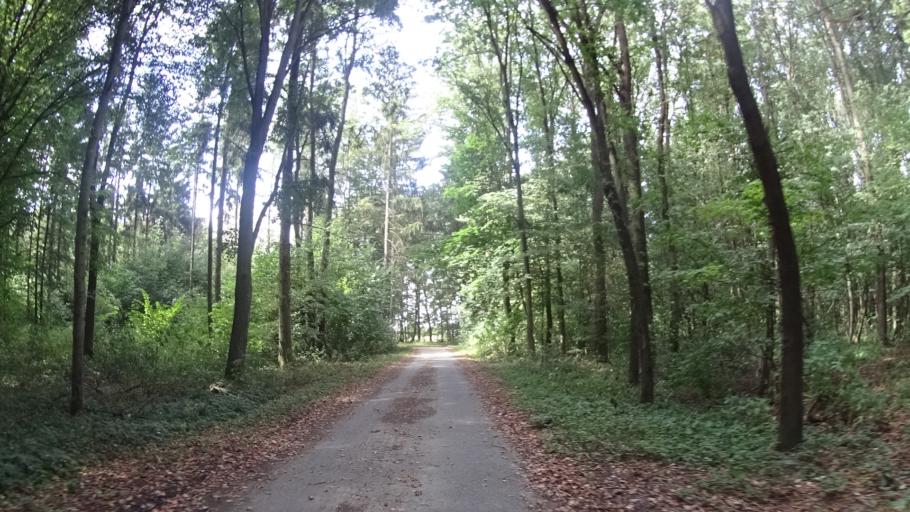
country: CZ
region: Olomoucky
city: Skrben
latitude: 49.6635
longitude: 17.1820
